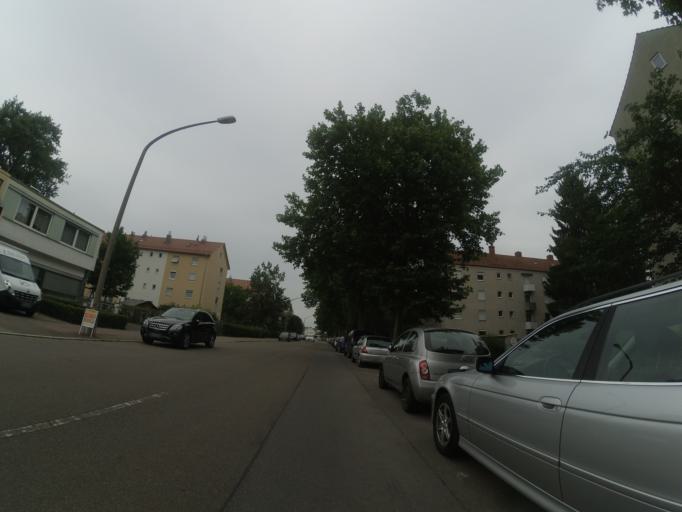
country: DE
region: Bavaria
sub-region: Swabia
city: Neu-Ulm
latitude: 48.3990
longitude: 10.0199
